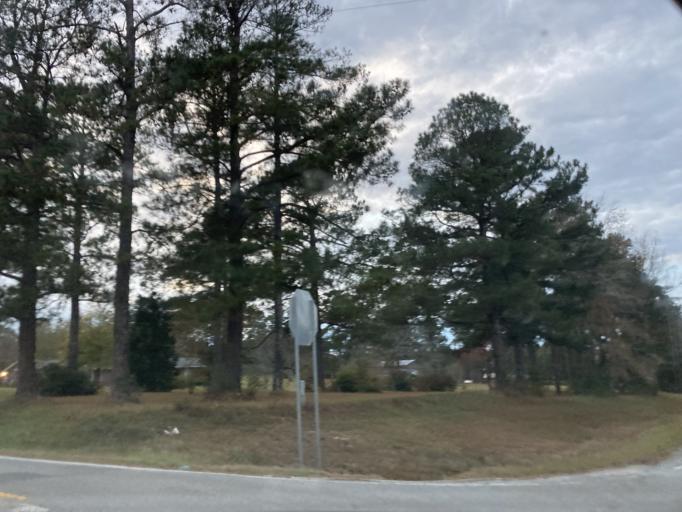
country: US
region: Georgia
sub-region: Jones County
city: Gray
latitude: 32.9807
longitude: -83.5085
